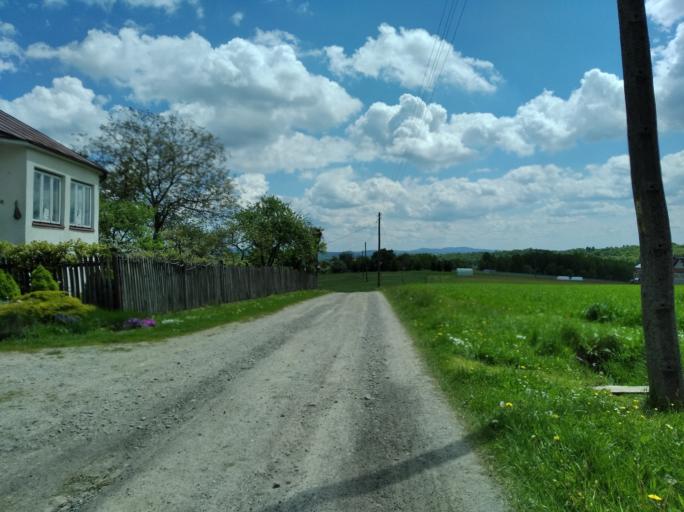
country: PL
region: Subcarpathian Voivodeship
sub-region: Powiat strzyzowski
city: Frysztak
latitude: 49.8346
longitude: 21.5680
